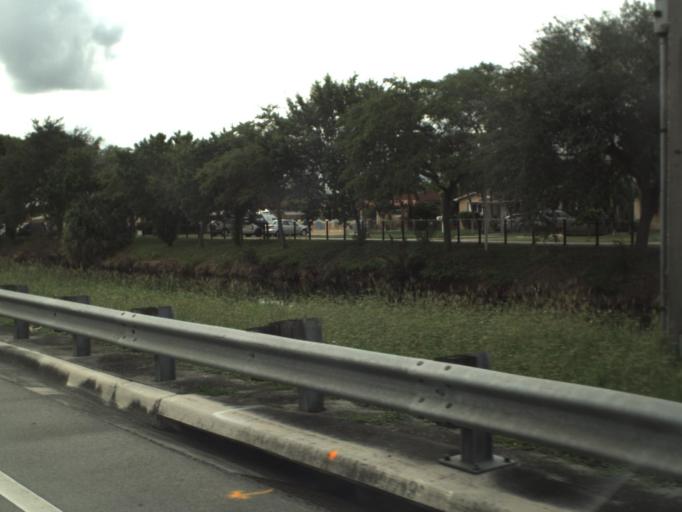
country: US
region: Florida
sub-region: Miami-Dade County
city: Sweetwater
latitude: 25.7613
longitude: -80.3765
